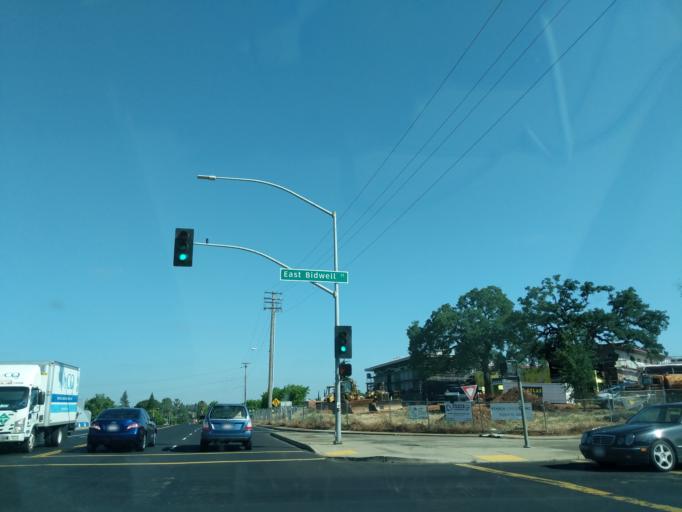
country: US
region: California
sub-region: Sacramento County
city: Folsom
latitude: 38.6727
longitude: -121.1714
